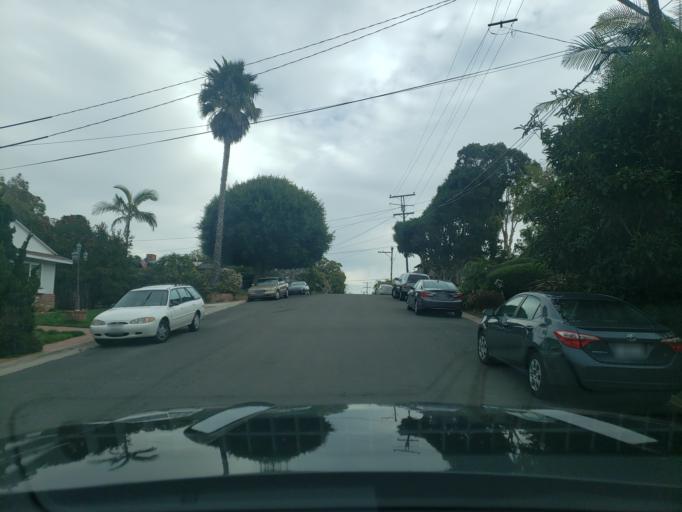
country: US
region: California
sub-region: San Diego County
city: Coronado
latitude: 32.7189
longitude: -117.2447
